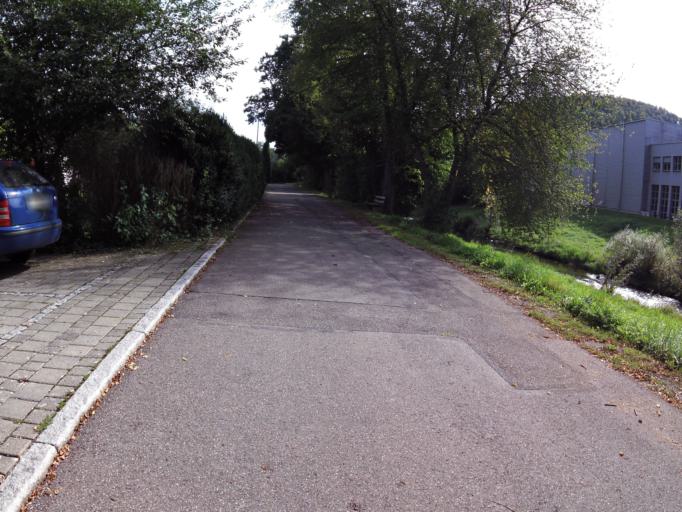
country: DE
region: Baden-Wuerttemberg
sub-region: Freiburg Region
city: Oberndorf
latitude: 48.3110
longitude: 8.5717
